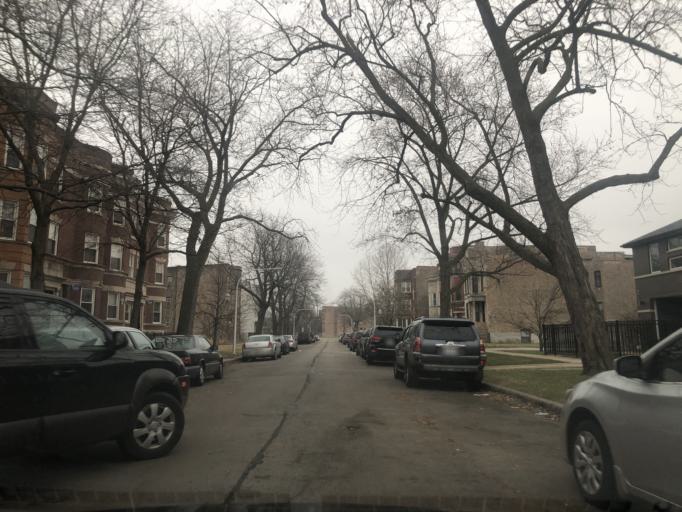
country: US
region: Illinois
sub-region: Cook County
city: Chicago
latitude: 41.7822
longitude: -87.5995
